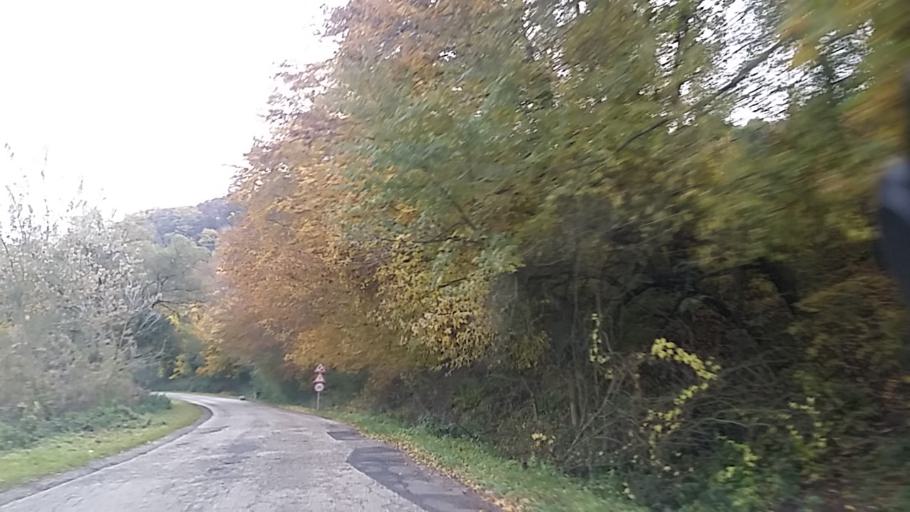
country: HU
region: Borsod-Abauj-Zemplen
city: Sajokaza
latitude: 48.2710
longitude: 20.5189
